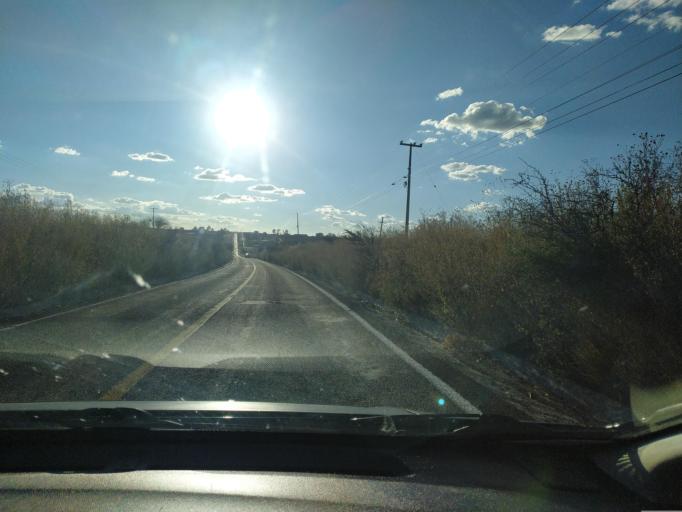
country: MX
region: Jalisco
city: San Diego de Alejandria
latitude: 21.0185
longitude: -101.9538
